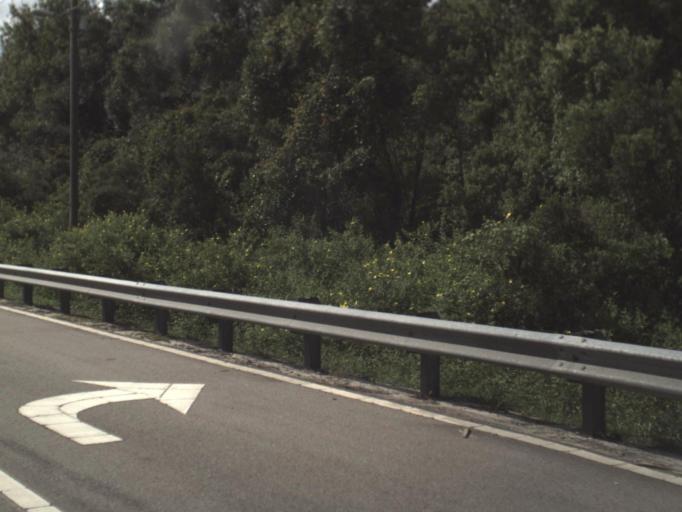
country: US
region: Florida
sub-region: Hillsborough County
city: Wimauma
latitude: 27.4598
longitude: -82.1397
